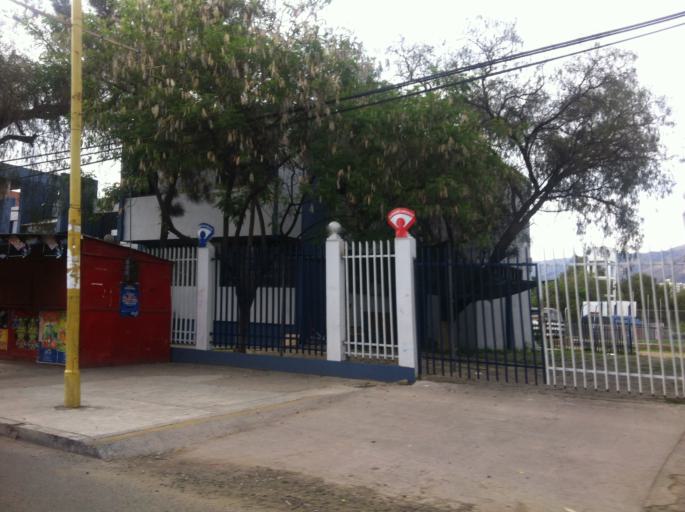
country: BO
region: Cochabamba
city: Cochabamba
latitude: -17.3798
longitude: -66.1452
